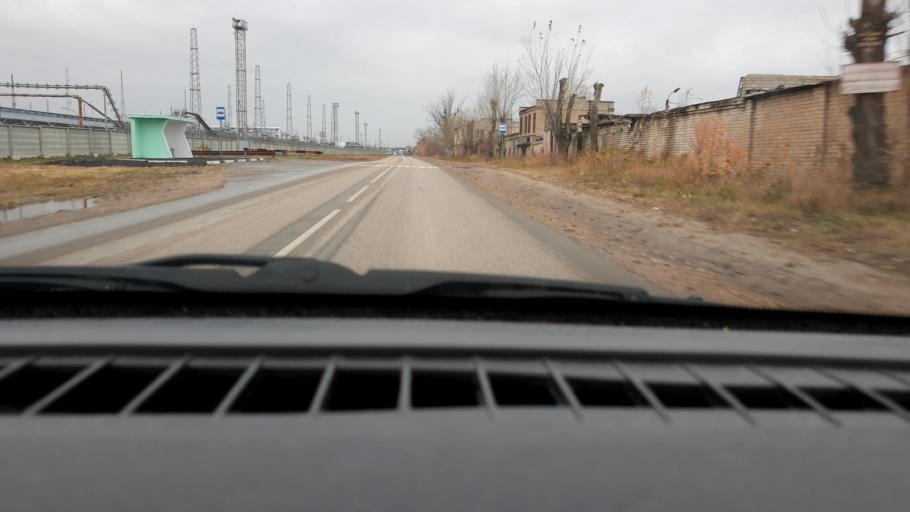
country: RU
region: Nizjnij Novgorod
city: Kstovo
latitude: 56.1190
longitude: 44.1451
